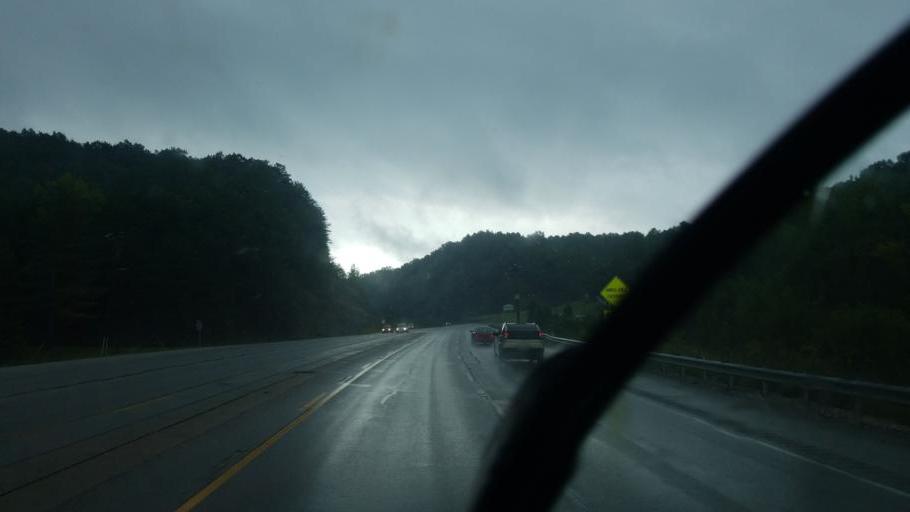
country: US
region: Kentucky
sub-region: Rowan County
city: Morehead
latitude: 38.1832
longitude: -83.4700
